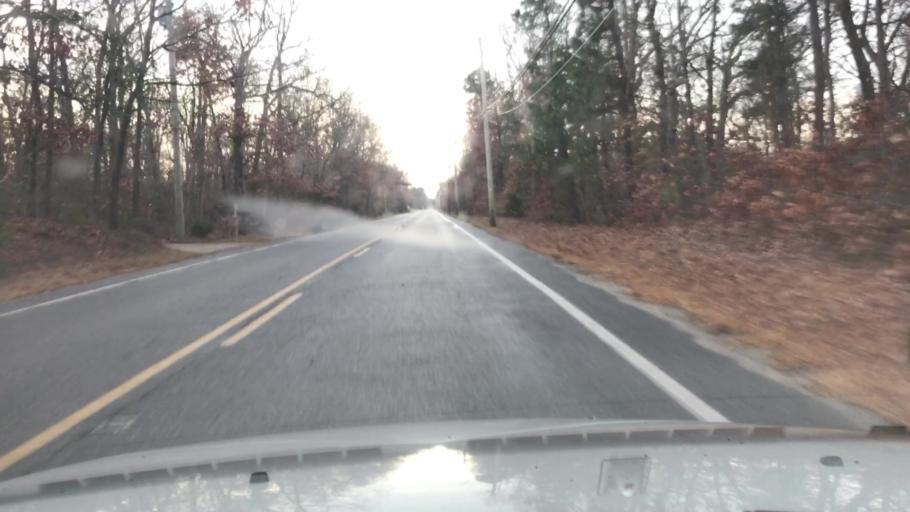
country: US
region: New Jersey
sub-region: Cape May County
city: Sea Isle City
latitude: 39.1894
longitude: -74.7576
